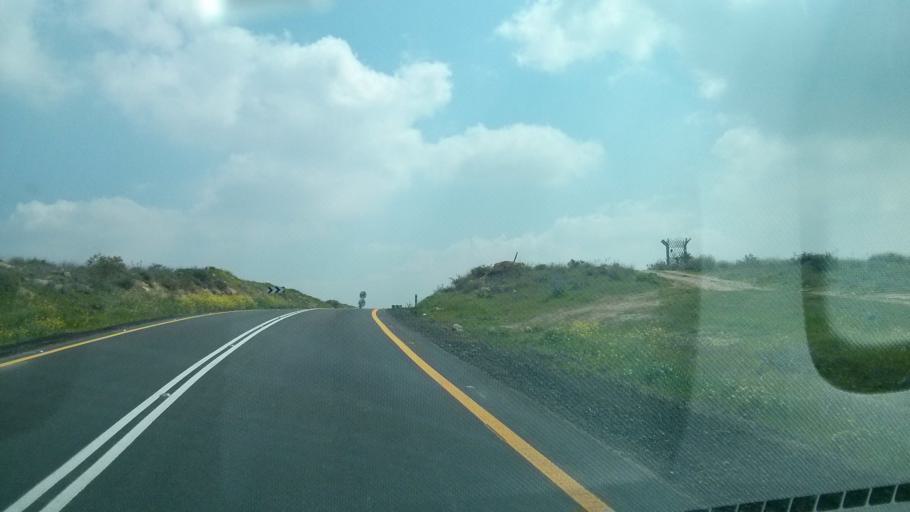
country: PS
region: West Bank
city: Ar Ramadin
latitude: 31.3499
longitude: 34.9109
